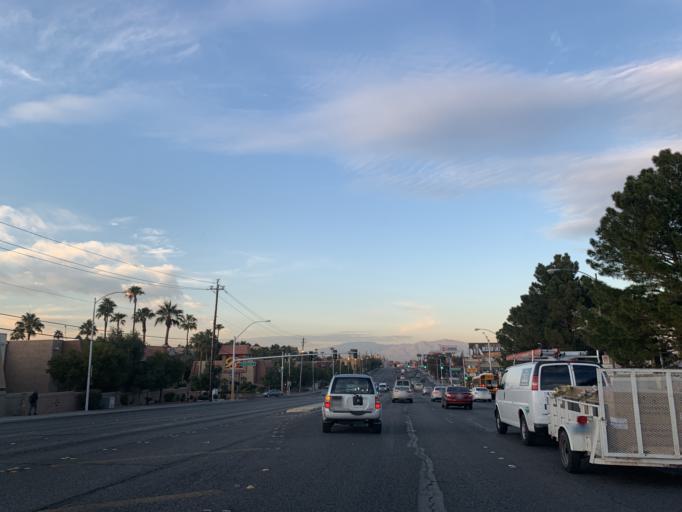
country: US
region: Nevada
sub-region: Clark County
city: Spring Valley
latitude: 36.1090
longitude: -115.2080
